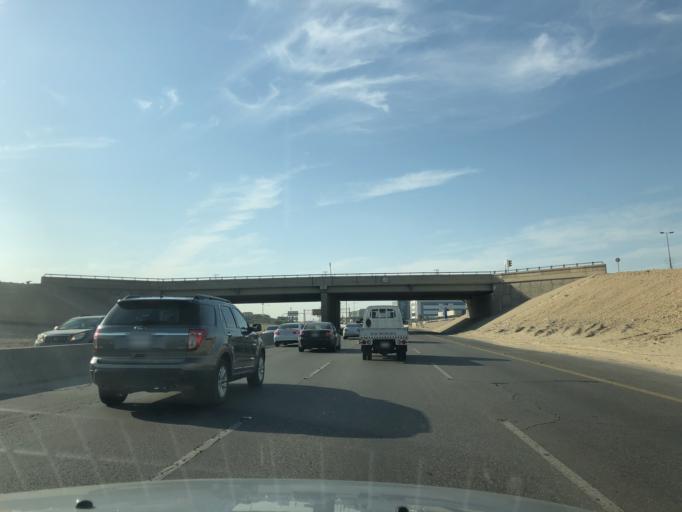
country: SA
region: Eastern Province
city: Dhahran
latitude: 26.3279
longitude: 50.1426
